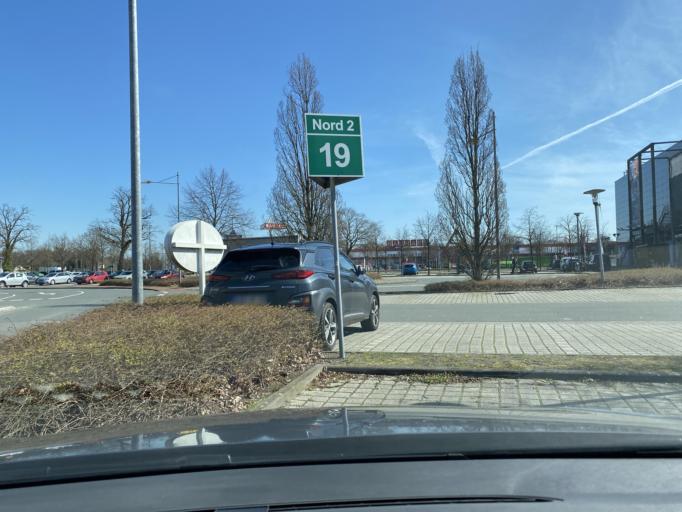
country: DE
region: Lower Saxony
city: Oyten
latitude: 53.0528
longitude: 8.9596
